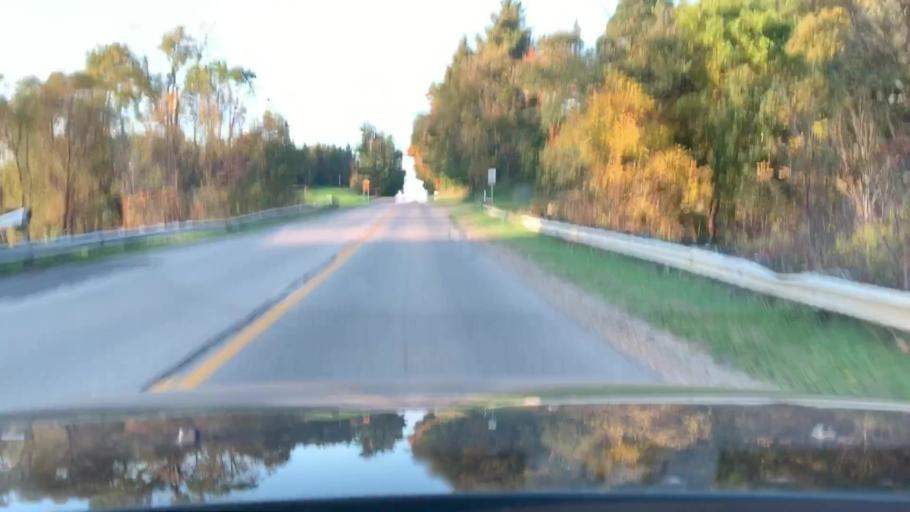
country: US
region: Michigan
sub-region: Ottawa County
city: Hudsonville
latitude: 42.7789
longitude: -85.8417
